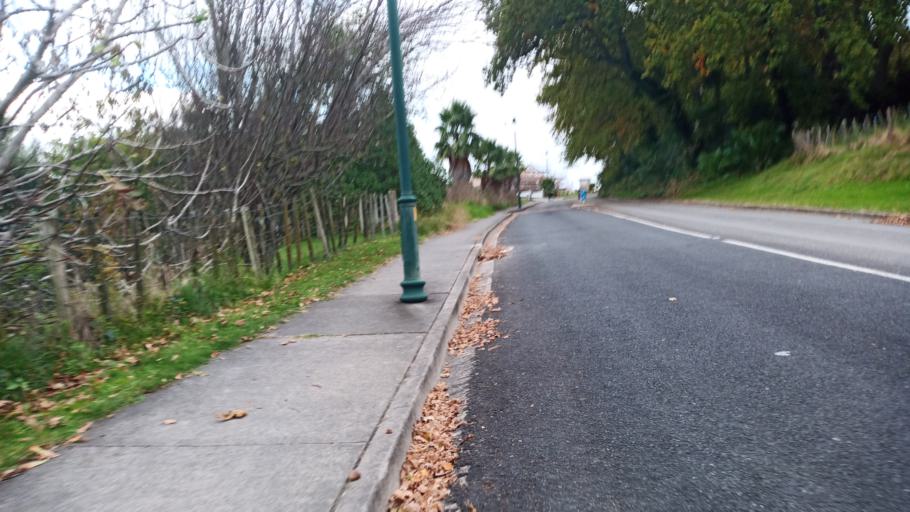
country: NZ
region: Gisborne
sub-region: Gisborne District
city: Gisborne
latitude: -38.6432
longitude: 178.0174
